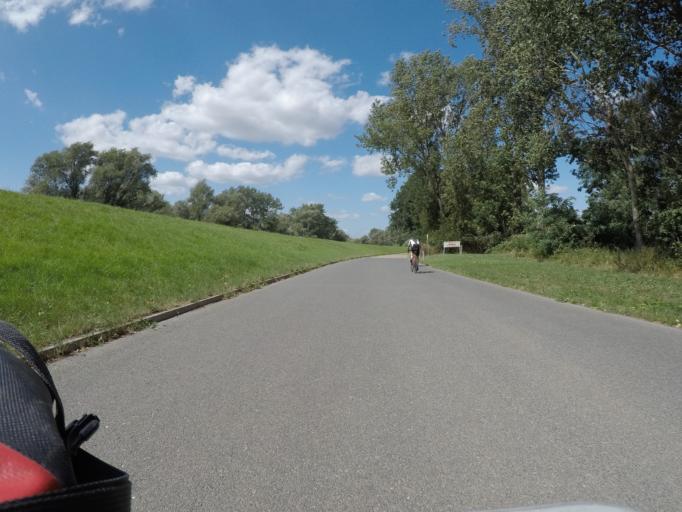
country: DE
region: Hamburg
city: Rothenburgsort
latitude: 53.5014
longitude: 10.0688
